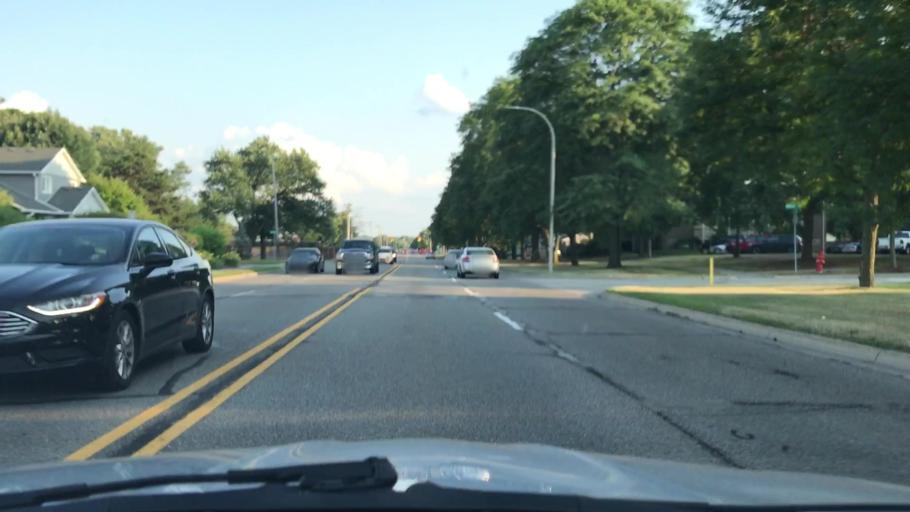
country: US
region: Michigan
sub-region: Oakland County
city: Clawson
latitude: 42.5283
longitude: -83.1653
